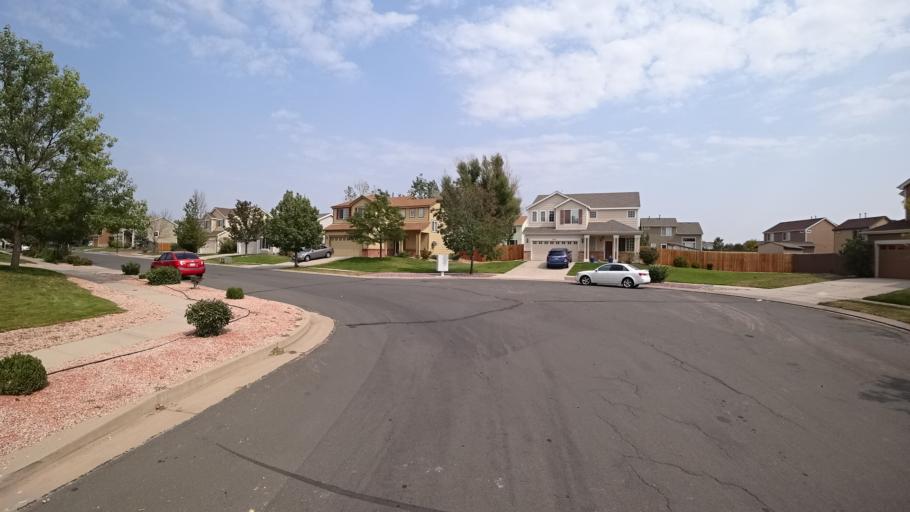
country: US
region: Colorado
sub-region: El Paso County
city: Cimarron Hills
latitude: 38.8232
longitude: -104.7325
